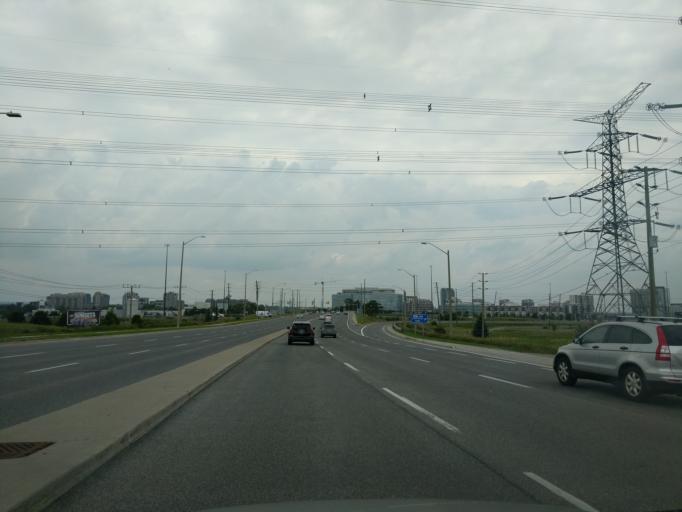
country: CA
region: Ontario
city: Markham
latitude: 43.8417
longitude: -79.3302
